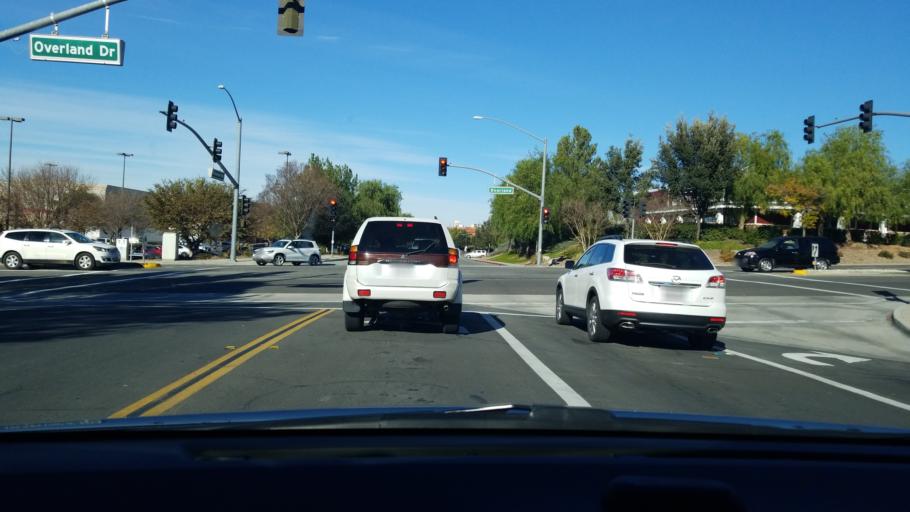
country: US
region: California
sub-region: Riverside County
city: Temecula
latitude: 33.5196
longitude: -117.1532
